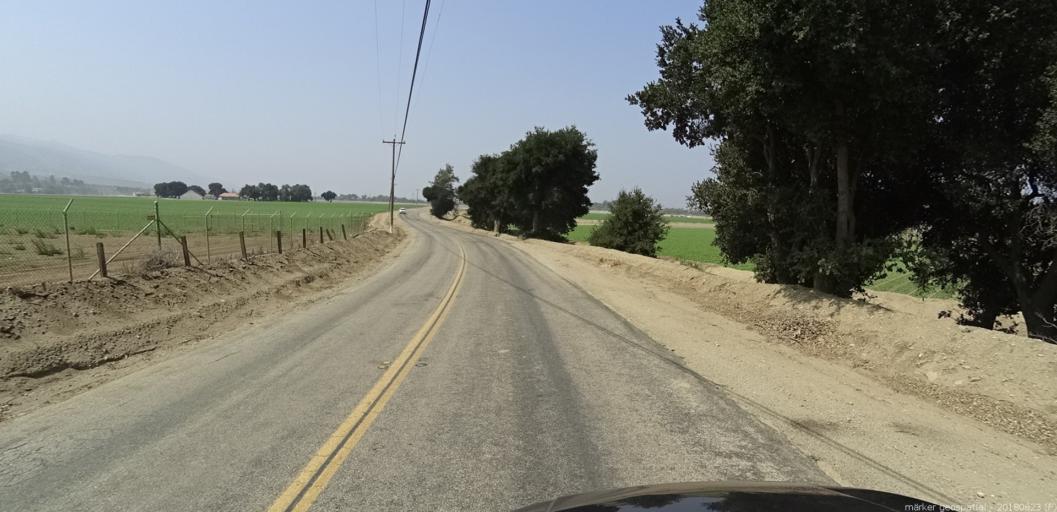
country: US
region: California
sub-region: Monterey County
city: Gonzales
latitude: 36.4757
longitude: -121.4714
